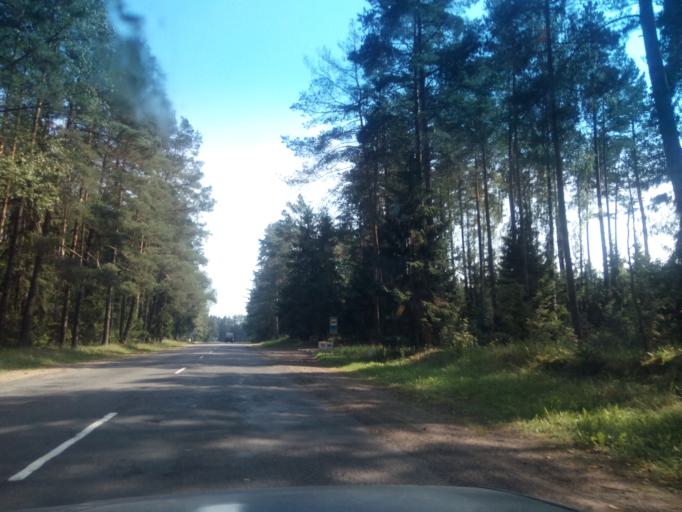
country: BY
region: Vitebsk
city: Vyerkhnyadzvinsk
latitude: 55.7940
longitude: 27.9658
